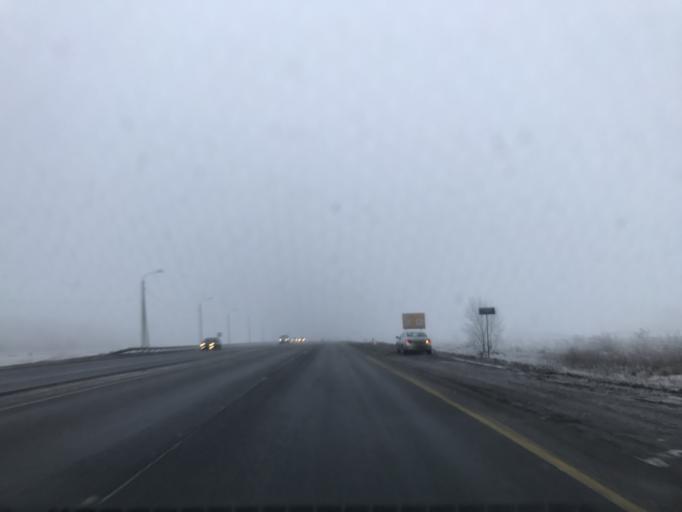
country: RU
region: Rostov
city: Grushevskaya
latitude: 47.4156
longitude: 39.9751
